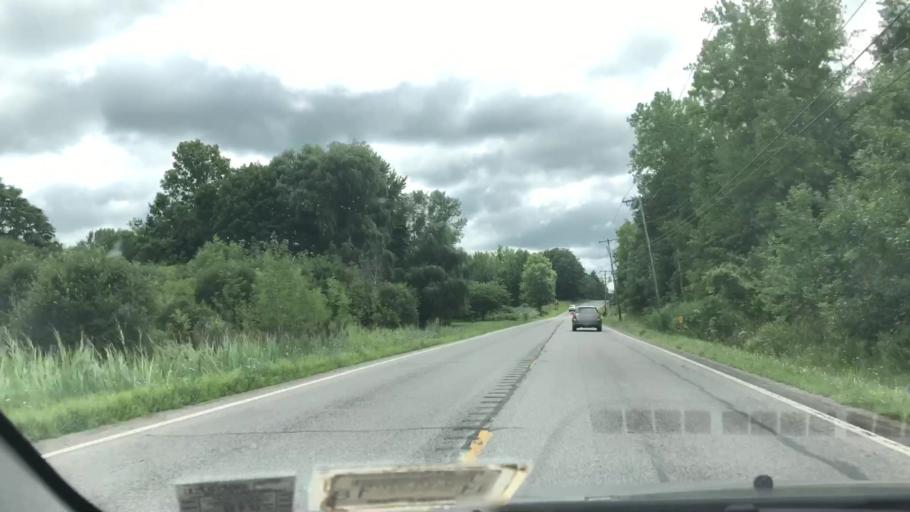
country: US
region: New York
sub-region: Wayne County
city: Macedon
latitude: 43.1252
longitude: -77.2927
